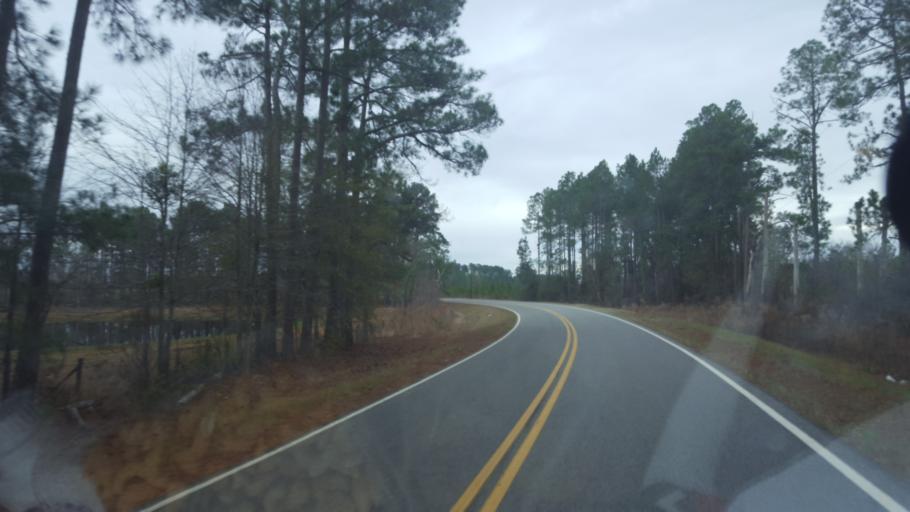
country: US
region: Georgia
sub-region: Wilcox County
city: Rochelle
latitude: 31.8103
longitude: -83.4613
